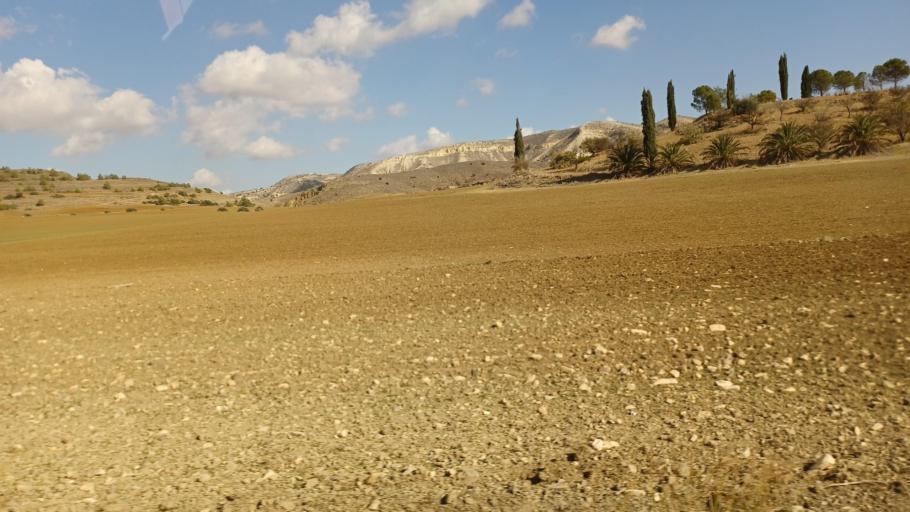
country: CY
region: Larnaka
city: Voroklini
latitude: 35.0113
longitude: 33.6417
